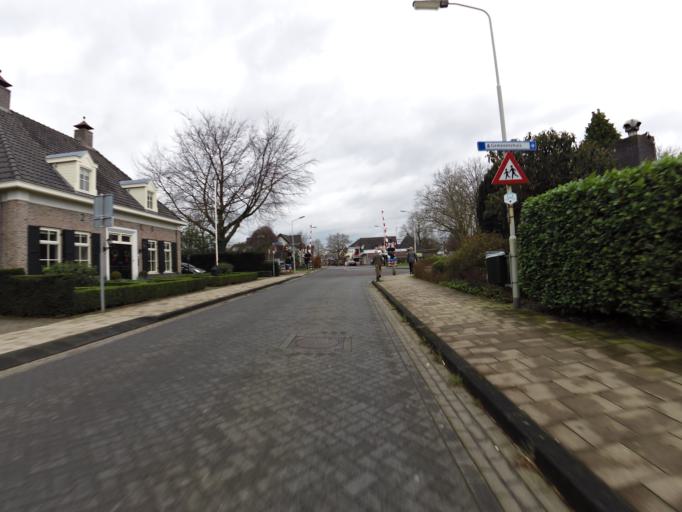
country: NL
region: Gelderland
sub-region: Gemeente Zevenaar
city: Zevenaar
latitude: 51.9325
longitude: 6.1313
